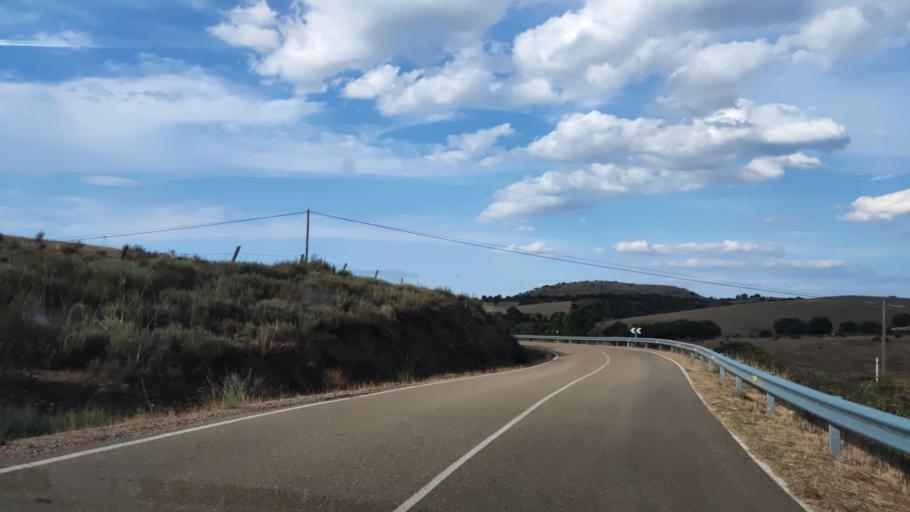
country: ES
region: Castille and Leon
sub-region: Provincia de Salamanca
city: Pastores
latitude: 40.5187
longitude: -6.5153
